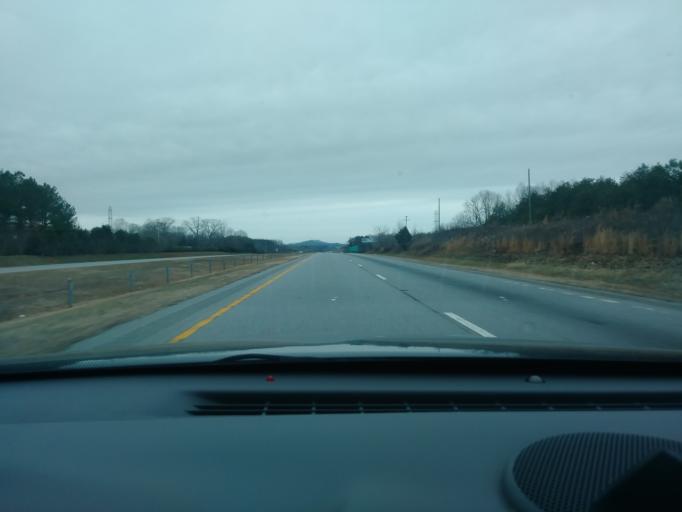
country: US
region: North Carolina
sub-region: Yadkin County
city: Jonesville
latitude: 36.1260
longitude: -80.8274
